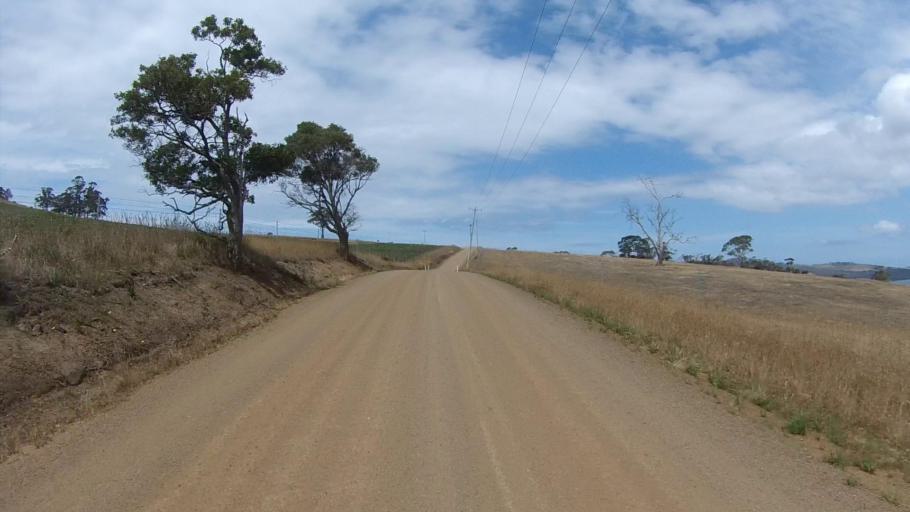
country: AU
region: Tasmania
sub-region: Kingborough
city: Blackmans Bay
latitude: -43.0549
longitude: 147.3154
